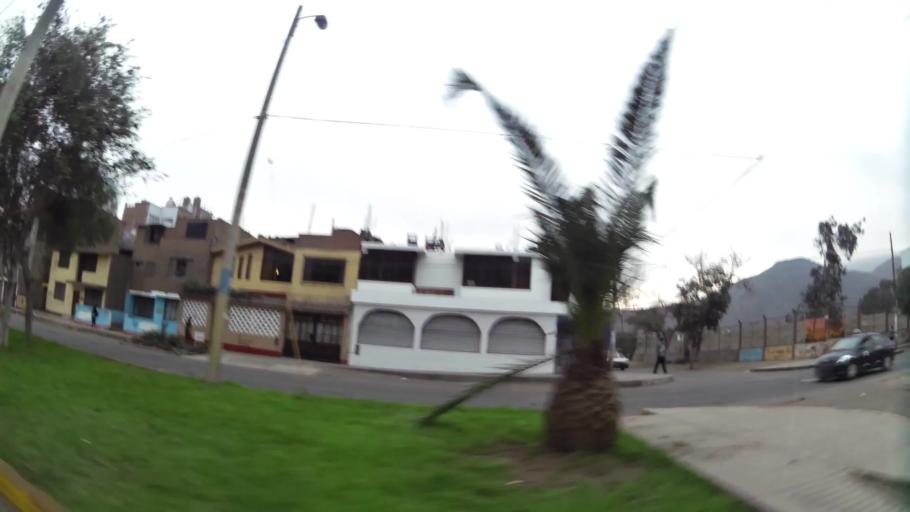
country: PE
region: Lima
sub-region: Lima
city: Vitarte
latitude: -12.0146
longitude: -76.9820
